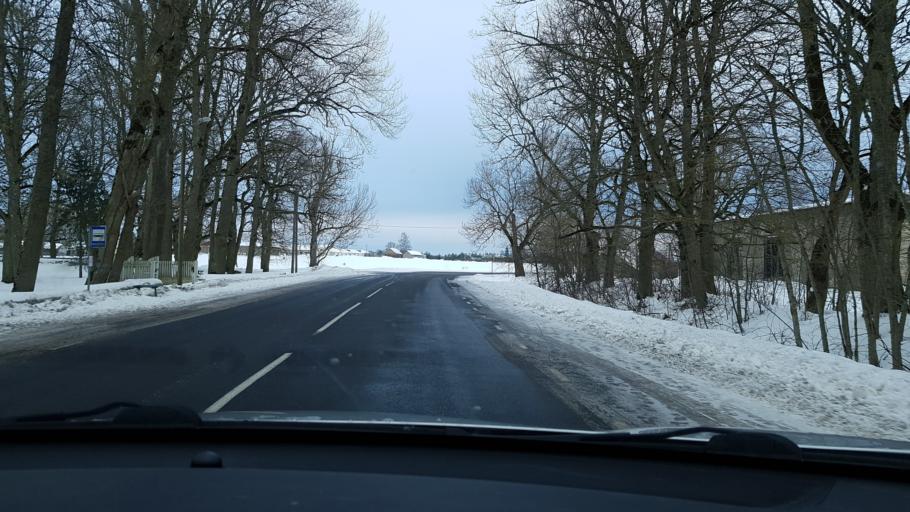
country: EE
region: Jaervamaa
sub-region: Paide linn
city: Paide
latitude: 58.8911
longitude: 25.7139
